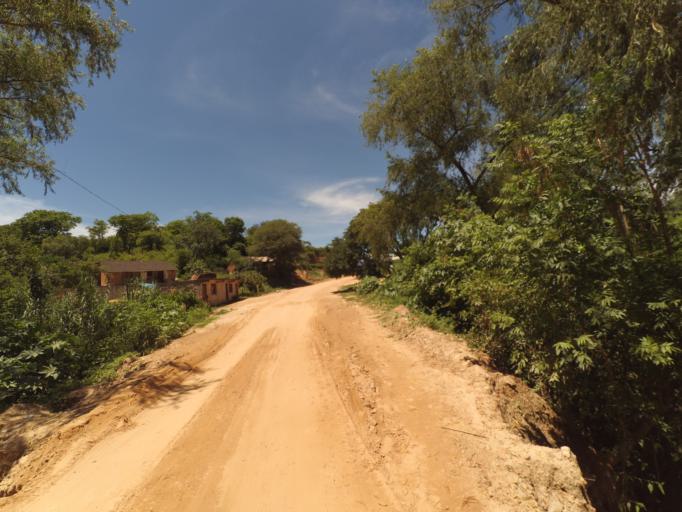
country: BO
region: Chuquisaca
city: Monteagudo
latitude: -19.8041
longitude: -63.9531
